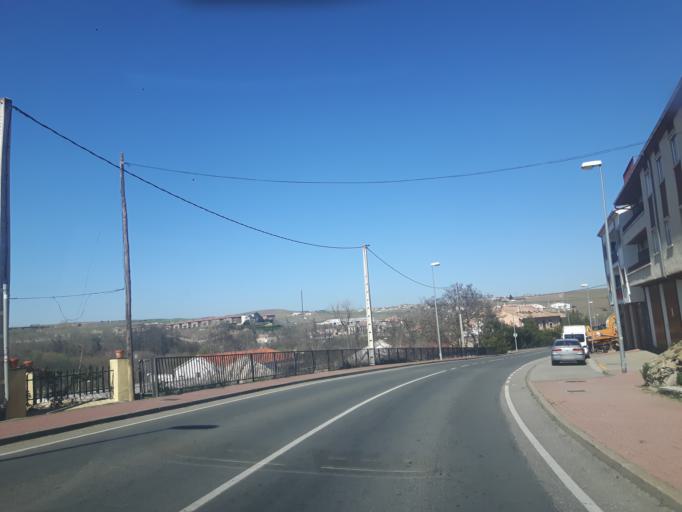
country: ES
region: Castille and Leon
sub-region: Provincia de Salamanca
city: Alba de Tormes
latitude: 40.8230
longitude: -5.5145
